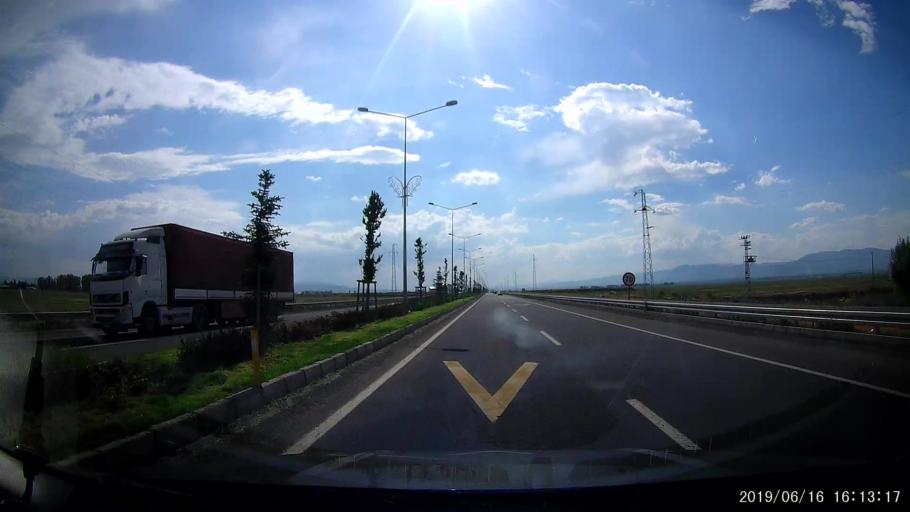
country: TR
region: Erzurum
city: Erzurum
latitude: 39.9594
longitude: 41.2752
